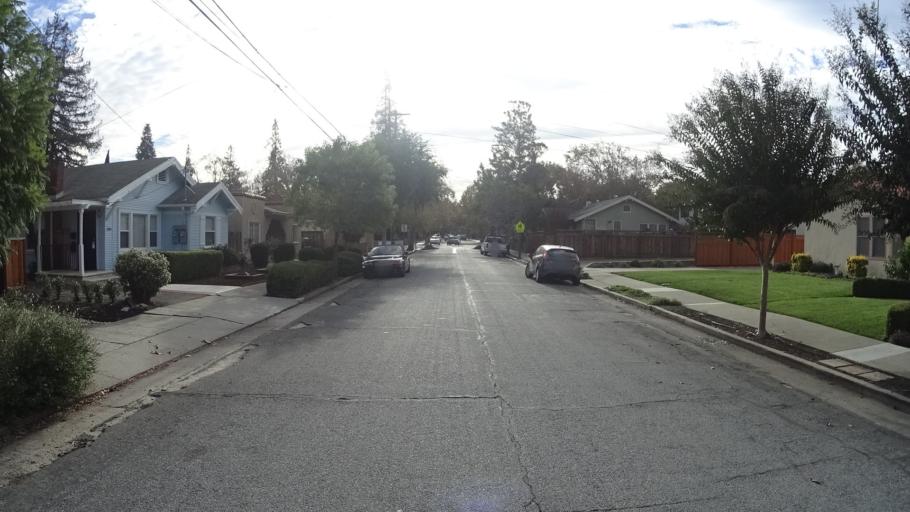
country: US
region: California
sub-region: Santa Clara County
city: Buena Vista
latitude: 37.3322
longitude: -121.9208
